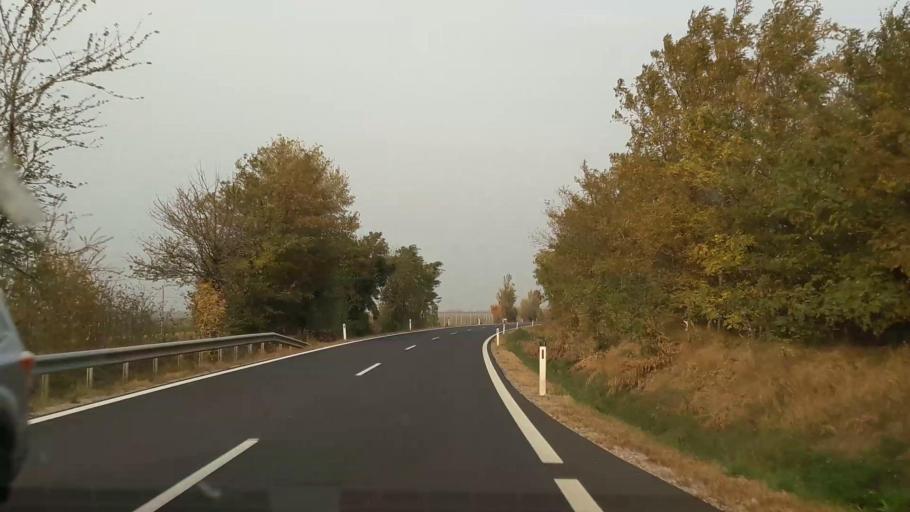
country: AT
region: Burgenland
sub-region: Politischer Bezirk Neusiedl am See
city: Gols
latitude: 47.9323
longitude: 16.9162
